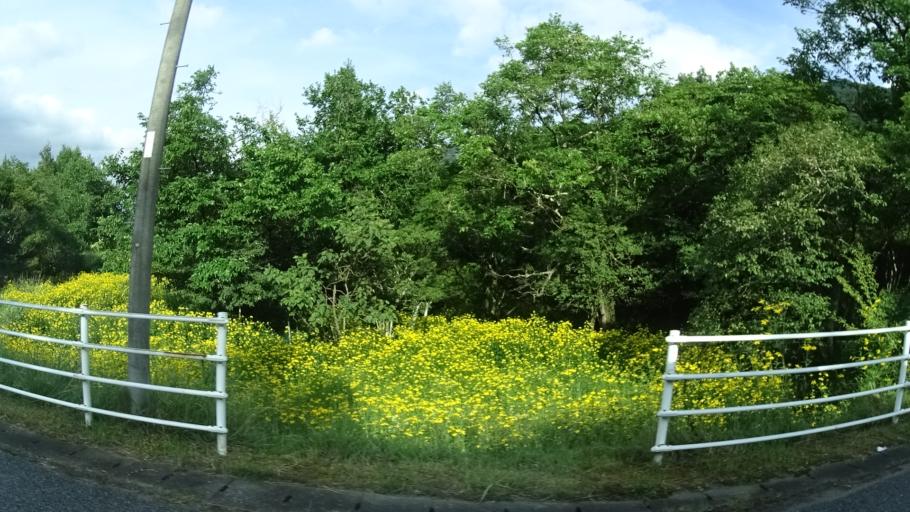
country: JP
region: Tochigi
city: Nikko
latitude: 36.7296
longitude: 139.5486
